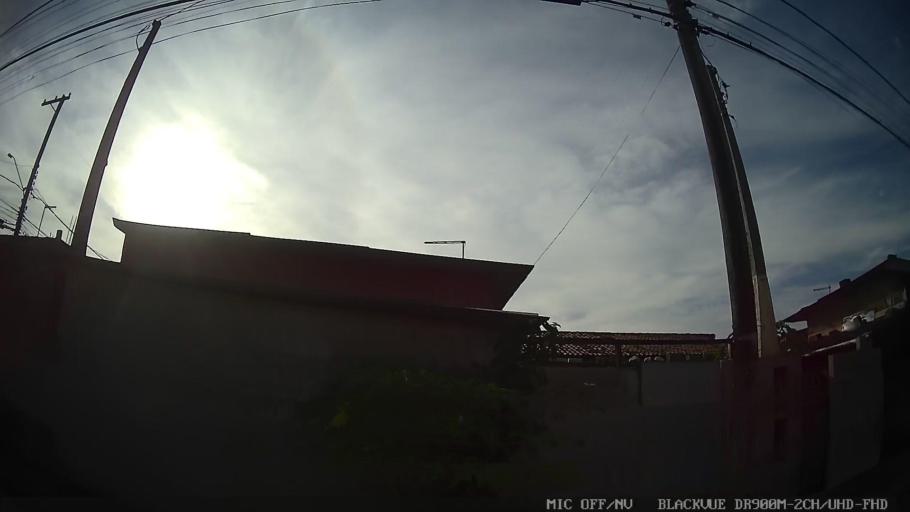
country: BR
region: Sao Paulo
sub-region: Itanhaem
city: Itanhaem
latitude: -24.1591
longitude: -46.7556
